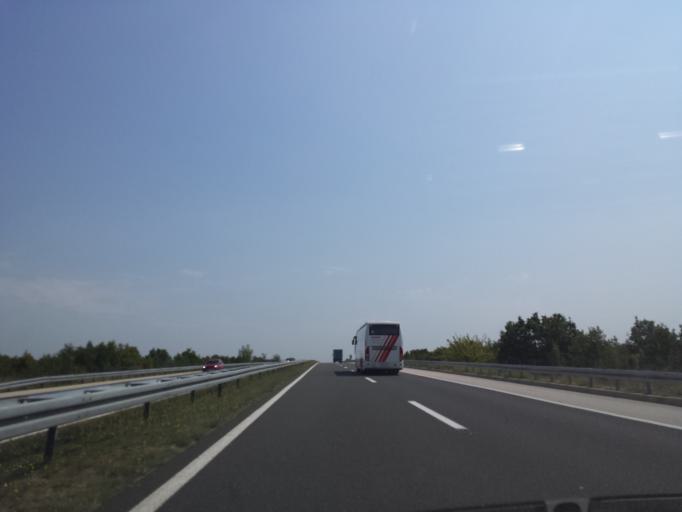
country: HR
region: Zadarska
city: Benkovac
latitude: 44.0049
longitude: 15.5953
